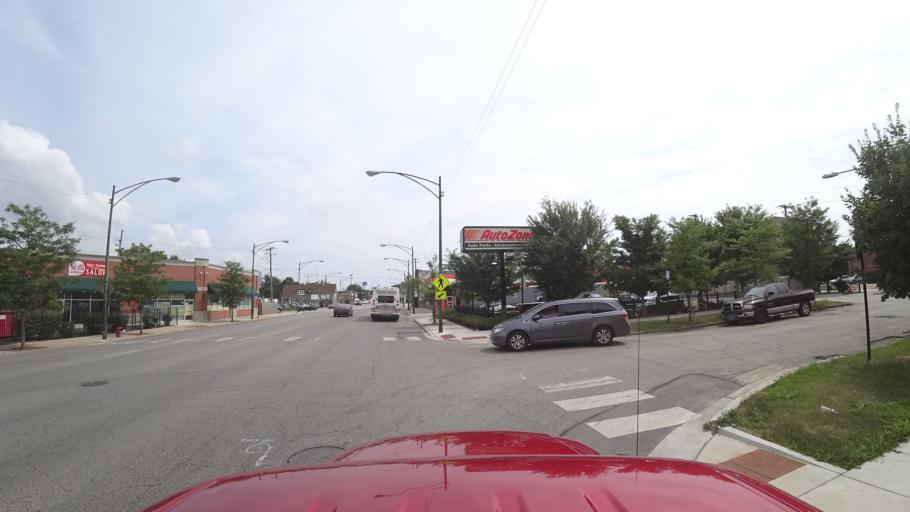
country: US
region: Illinois
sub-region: Cook County
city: Chicago
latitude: 41.8335
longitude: -87.6724
